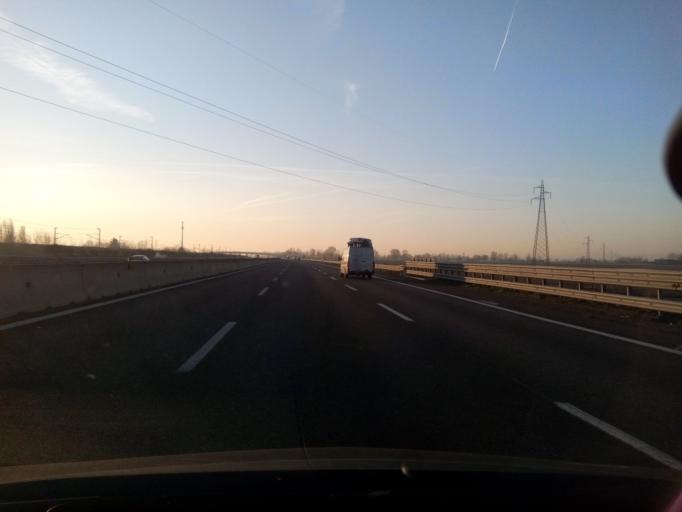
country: IT
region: Lombardy
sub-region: Provincia di Lodi
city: Lodi Vecchio
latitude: 45.3007
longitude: 9.4072
